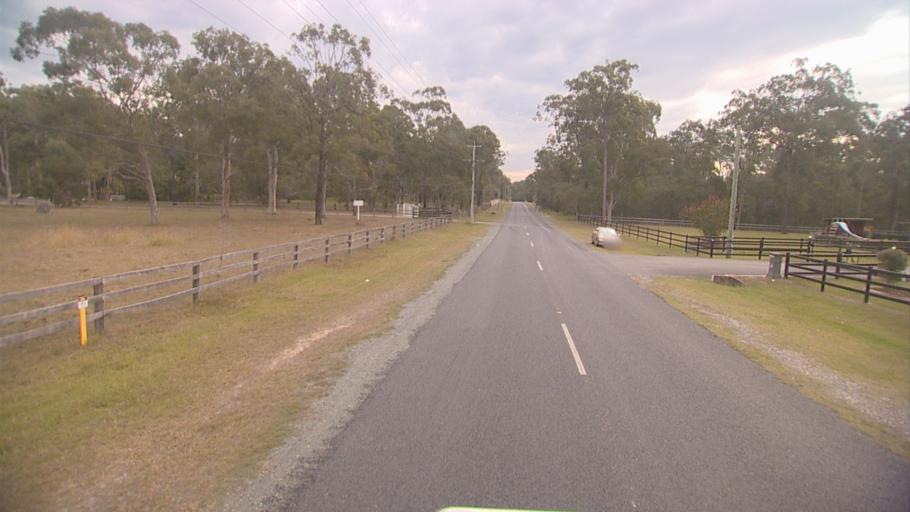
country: AU
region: Queensland
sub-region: Logan
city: Chambers Flat
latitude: -27.7842
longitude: 153.1159
